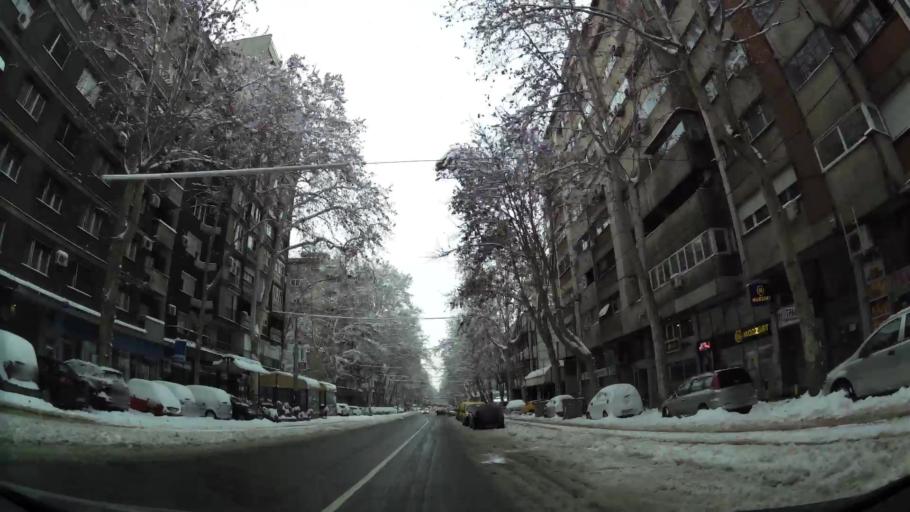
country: RS
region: Central Serbia
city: Belgrade
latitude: 44.8084
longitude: 20.4763
